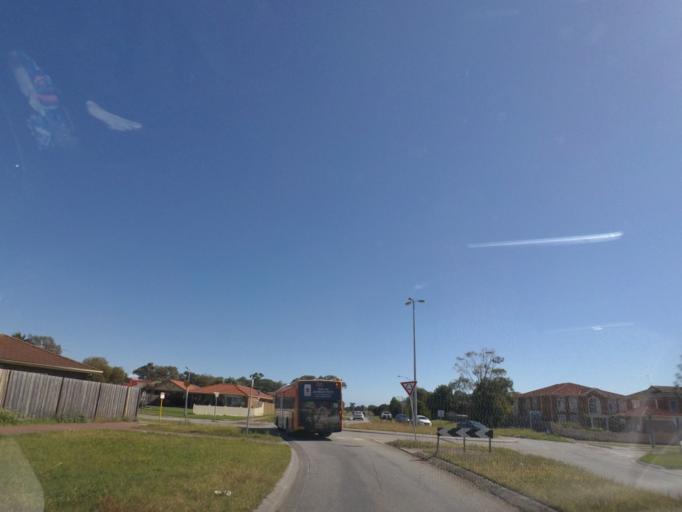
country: AU
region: Victoria
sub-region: Kingston
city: Chelsea Heights
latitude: -38.0295
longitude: 145.1292
